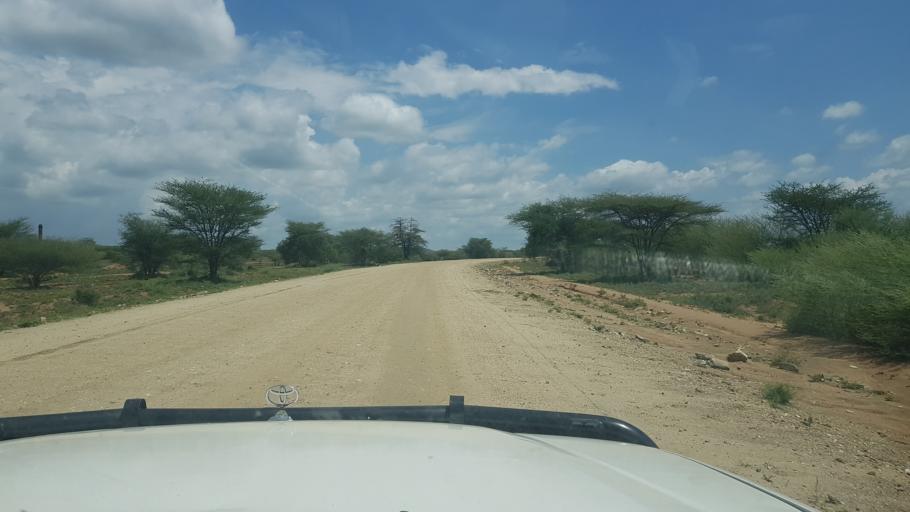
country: ET
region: Southern Nations, Nationalities, and People's Region
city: Turmi
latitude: 5.0797
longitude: 36.2410
